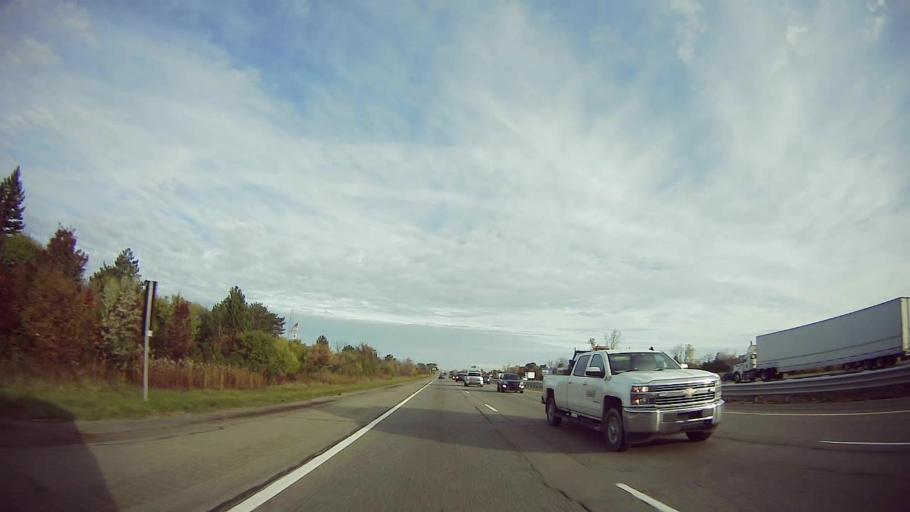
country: US
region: Michigan
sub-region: Oakland County
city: Clawson
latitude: 42.5438
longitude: -83.1167
